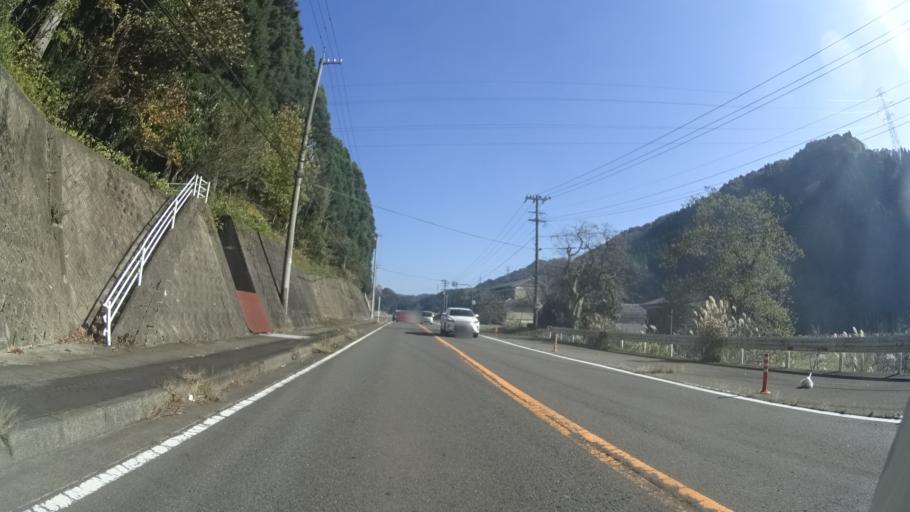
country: JP
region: Fukui
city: Ono
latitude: 35.9993
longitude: 136.4208
